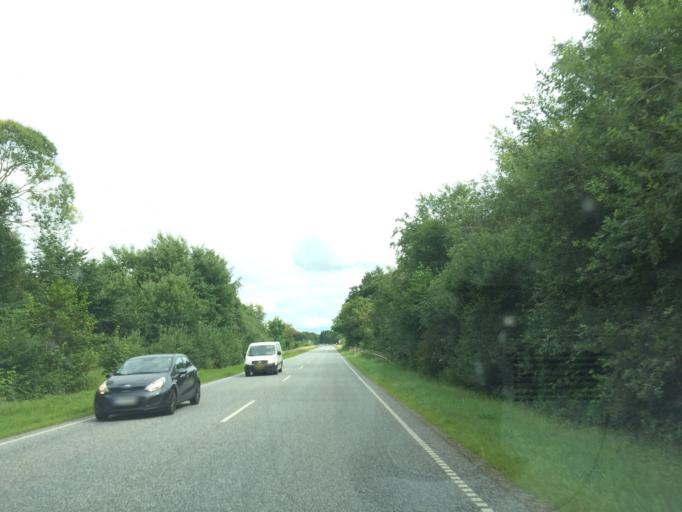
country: DK
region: Central Jutland
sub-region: Viborg Kommune
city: Bjerringbro
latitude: 56.3085
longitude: 9.5994
